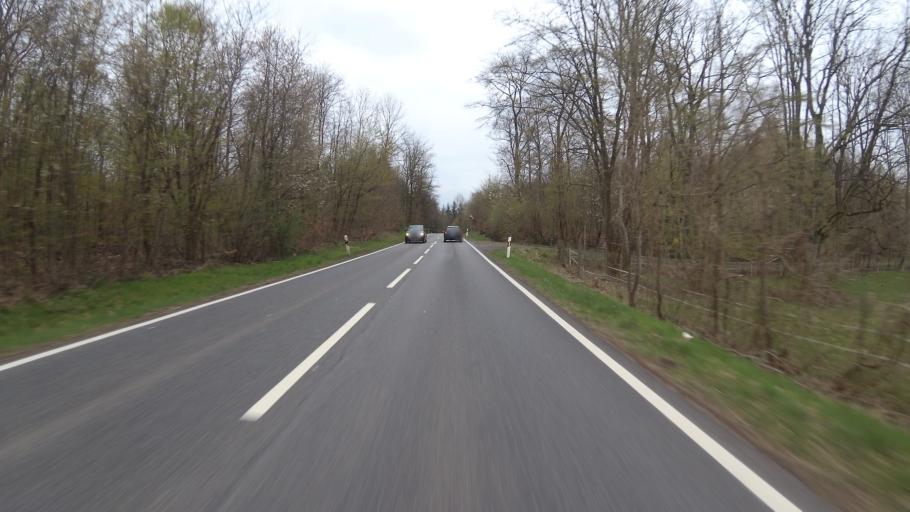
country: DE
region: Saarland
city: Sankt Ingbert
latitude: 49.2955
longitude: 7.0941
